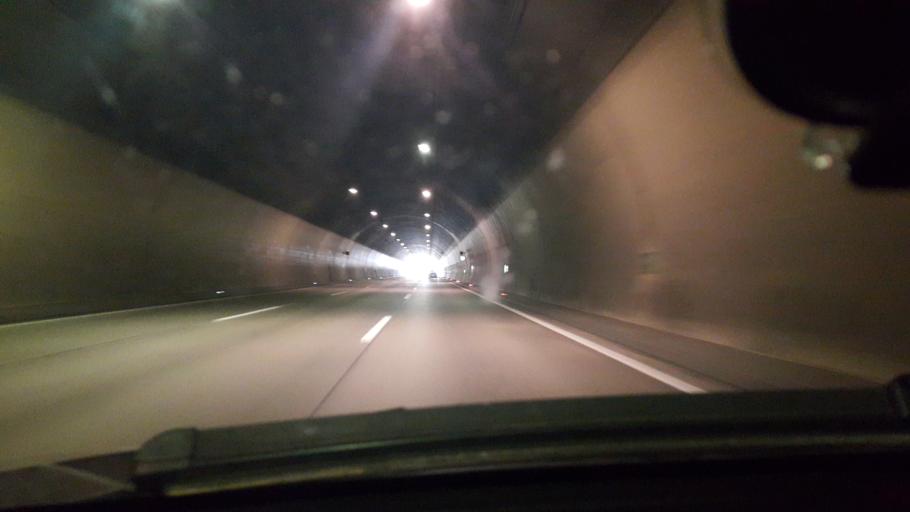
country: AT
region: Styria
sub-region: Politischer Bezirk Graz-Umgebung
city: Gratkorn
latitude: 47.1417
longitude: 15.3401
